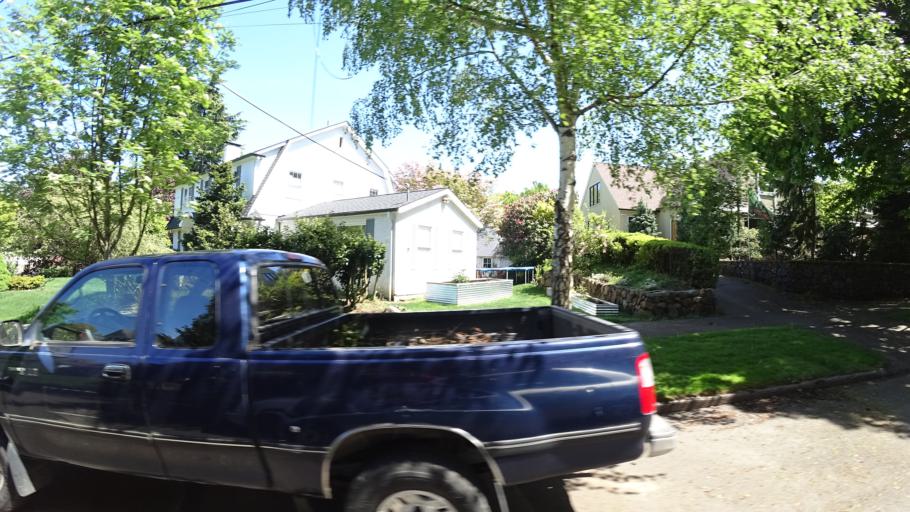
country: US
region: Oregon
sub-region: Clackamas County
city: Milwaukie
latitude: 45.4714
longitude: -122.6314
